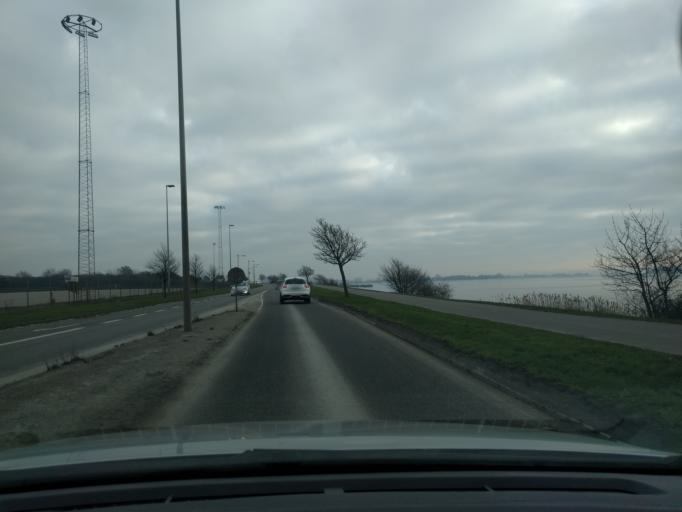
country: DK
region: Zealand
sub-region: Guldborgsund Kommune
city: Nykobing Falster
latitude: 54.7583
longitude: 11.8713
